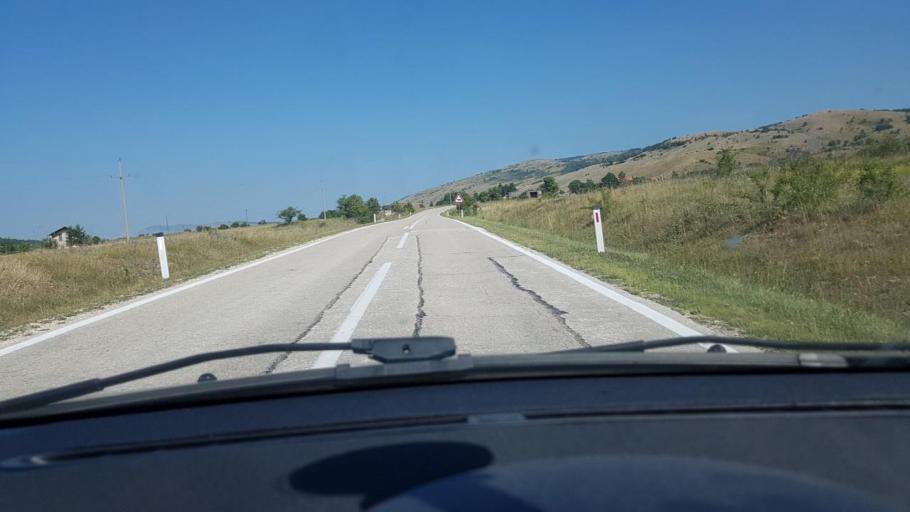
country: BA
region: Federation of Bosnia and Herzegovina
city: Bosansko Grahovo
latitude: 44.1142
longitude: 16.5394
